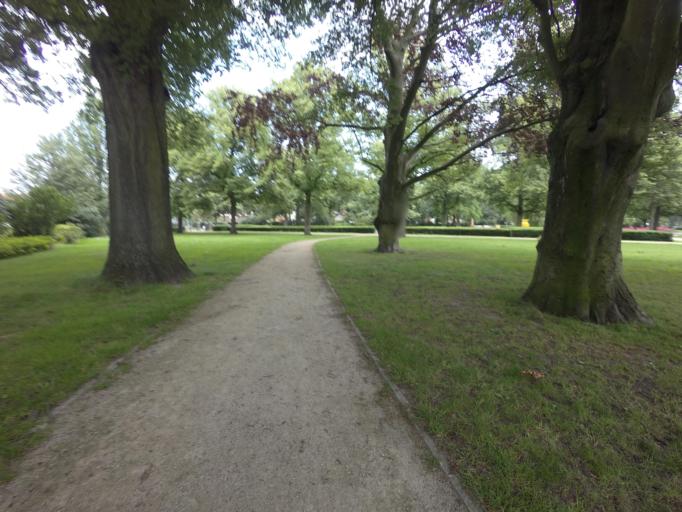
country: NL
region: South Holland
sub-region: Gemeente Schiedam
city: Schiedam
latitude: 51.9106
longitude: 4.3897
